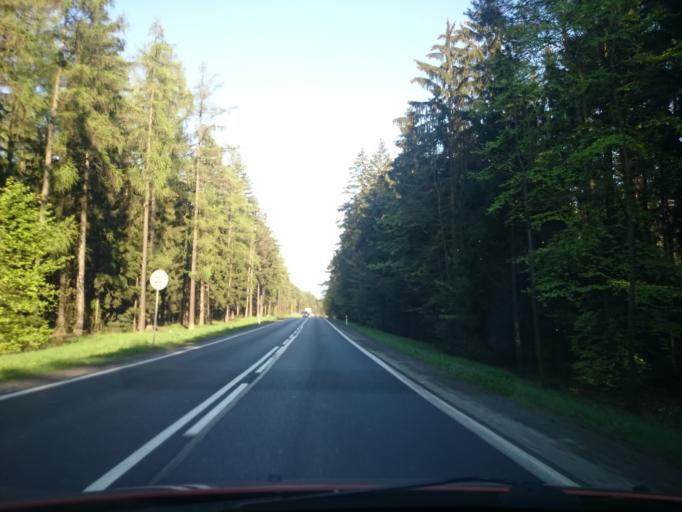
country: PL
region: Lower Silesian Voivodeship
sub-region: Powiat klodzki
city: Szczytna
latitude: 50.4253
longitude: 16.4819
